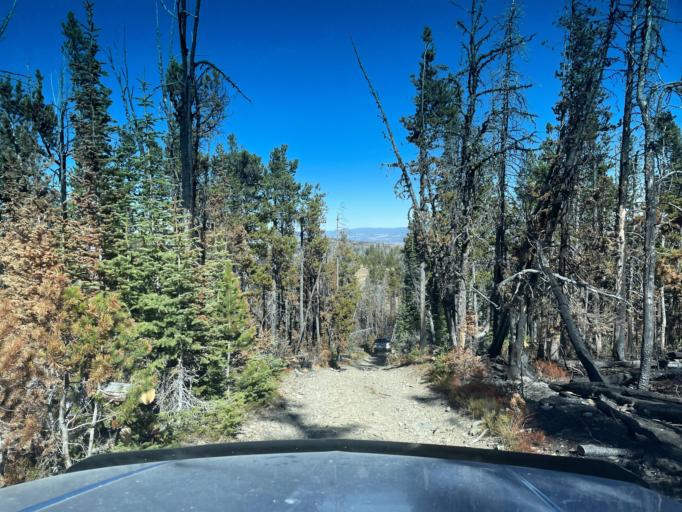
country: US
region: Montana
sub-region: Broadwater County
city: Townsend
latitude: 46.4821
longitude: -111.2563
